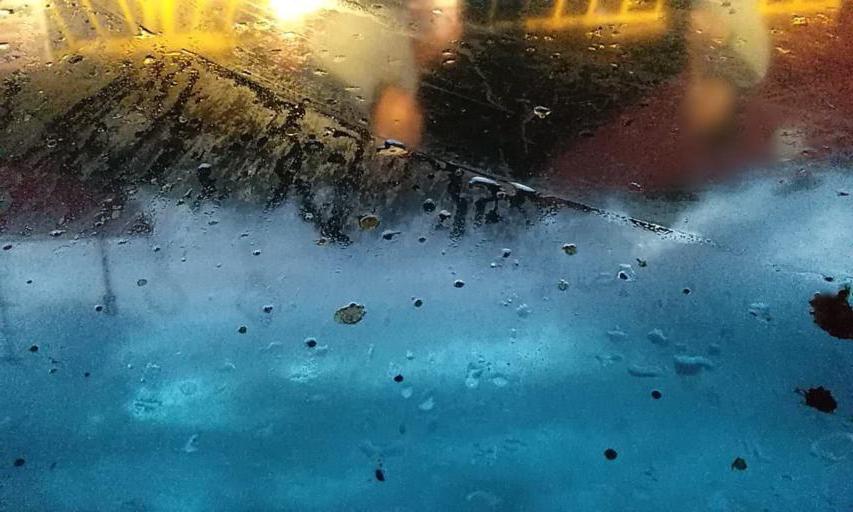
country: BR
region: Para
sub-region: Altamira
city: Altamira
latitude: -3.1246
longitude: -51.7013
